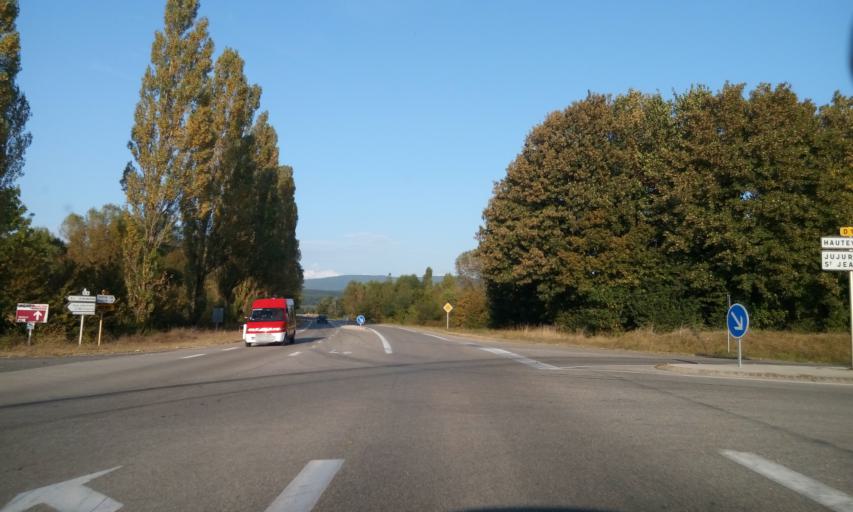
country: FR
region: Rhone-Alpes
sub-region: Departement de l'Ain
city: Ambronay
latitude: 46.0387
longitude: 5.3523
